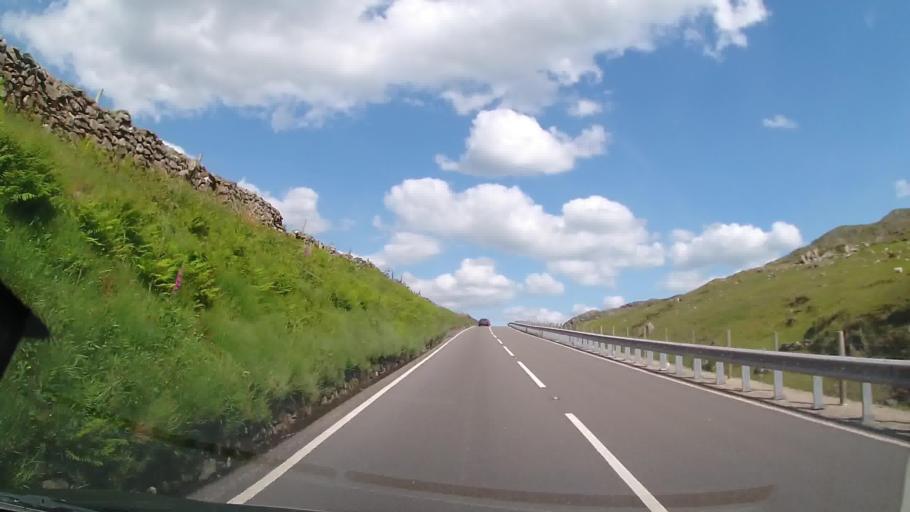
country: GB
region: Wales
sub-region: Gwynedd
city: Dolgellau
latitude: 52.7400
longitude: -3.7901
